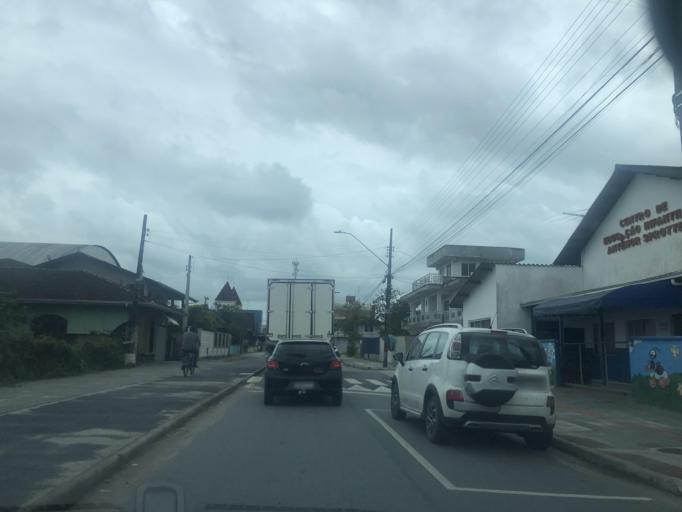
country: BR
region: Santa Catarina
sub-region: Joinville
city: Joinville
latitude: -26.3690
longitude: -48.7210
